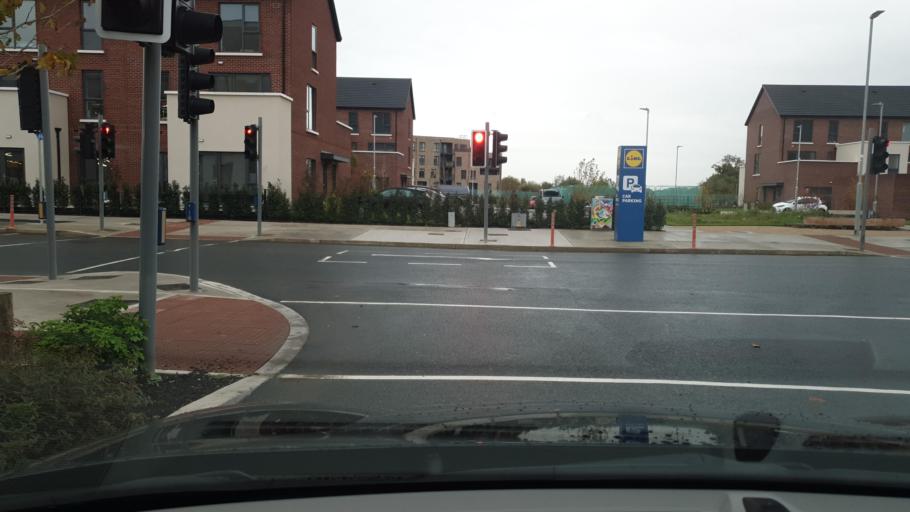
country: IE
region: Leinster
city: Lucan
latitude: 53.3462
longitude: -6.4737
